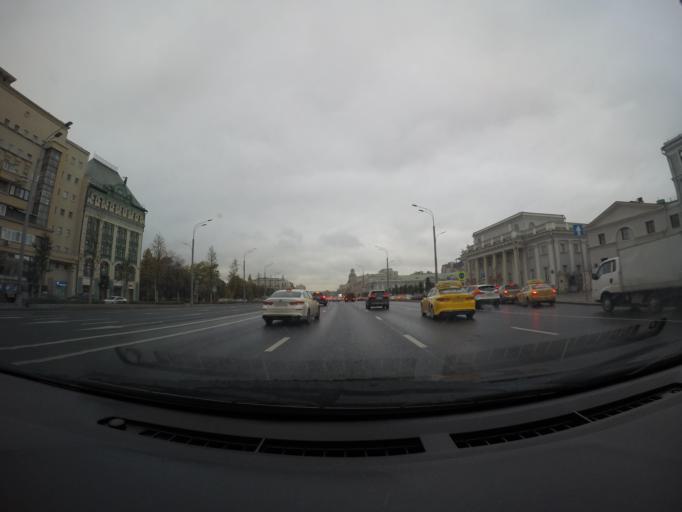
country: RU
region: Moscow
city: Moscow
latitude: 55.7723
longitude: 37.6369
